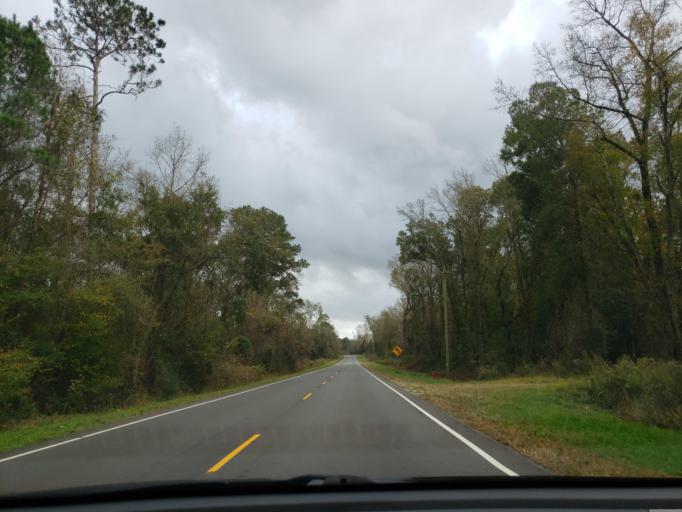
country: US
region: North Carolina
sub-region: Duplin County
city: Kenansville
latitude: 34.8772
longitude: -77.8932
